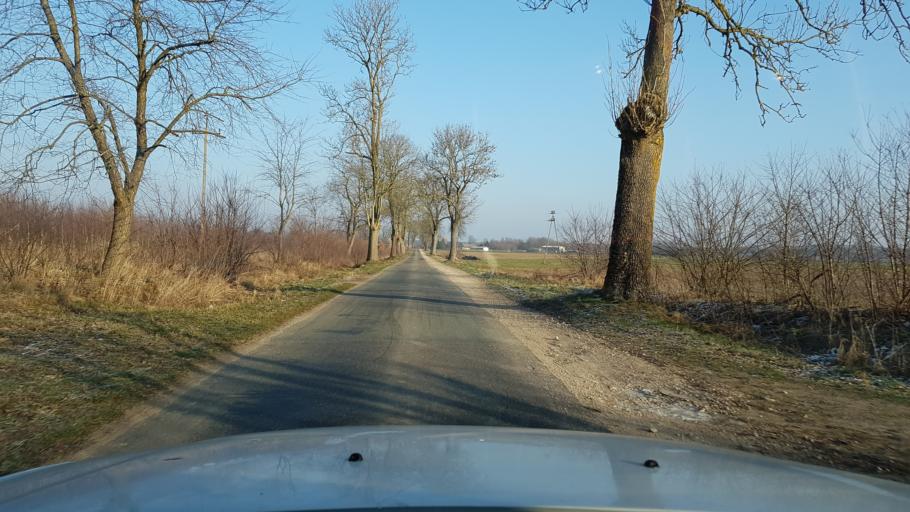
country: PL
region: West Pomeranian Voivodeship
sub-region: Powiat bialogardzki
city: Bialogard
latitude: 54.0636
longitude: 16.0831
